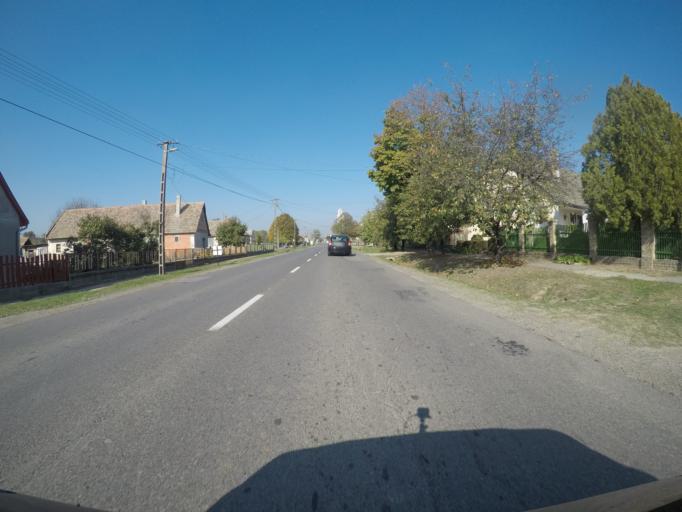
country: HU
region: Tolna
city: Szedres
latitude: 46.4728
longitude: 18.6849
